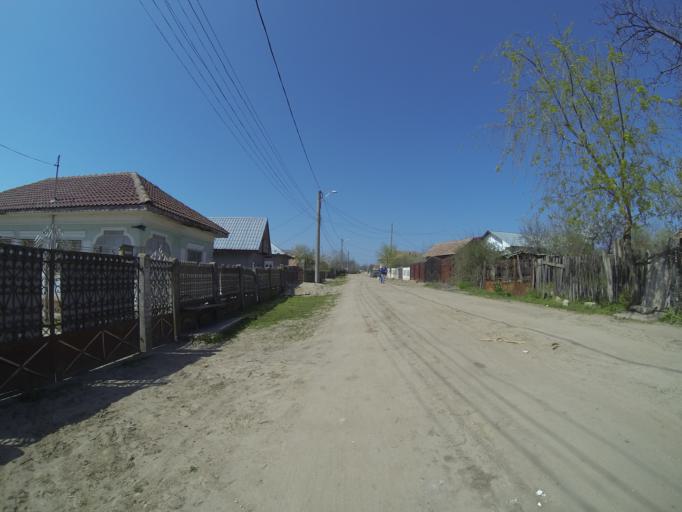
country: RO
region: Dolj
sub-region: Comuna Segarcea
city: Segarcea
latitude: 44.1003
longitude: 23.7305
